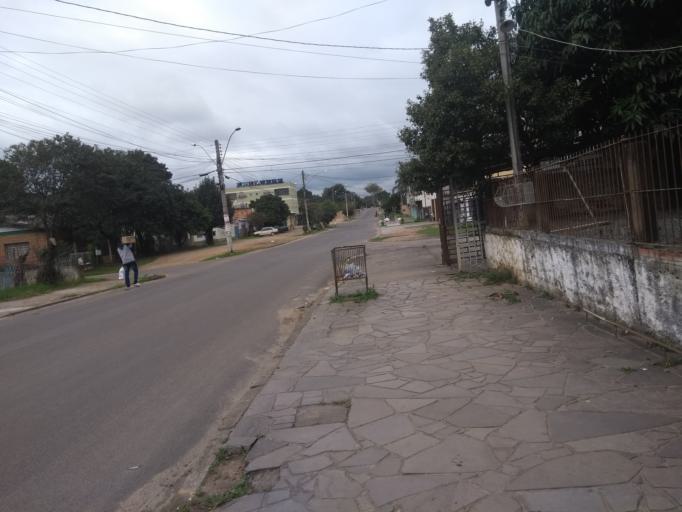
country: BR
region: Rio Grande do Sul
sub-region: Cachoeirinha
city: Cachoeirinha
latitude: -30.0002
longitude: -51.0748
